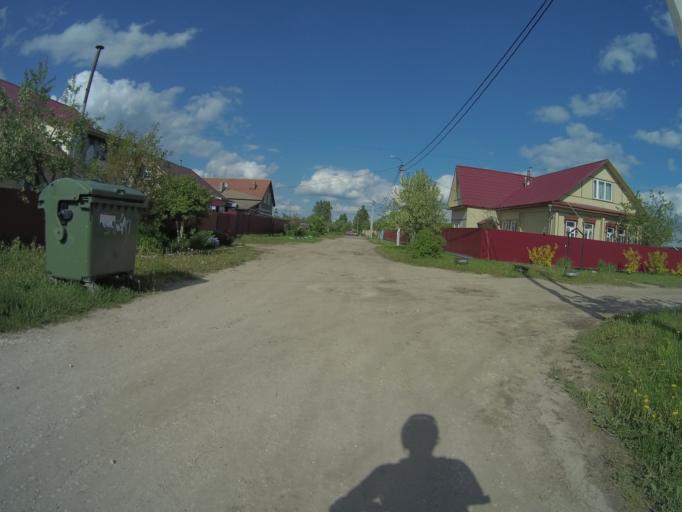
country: RU
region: Vladimir
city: Suzdal'
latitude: 56.4138
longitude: 40.4300
